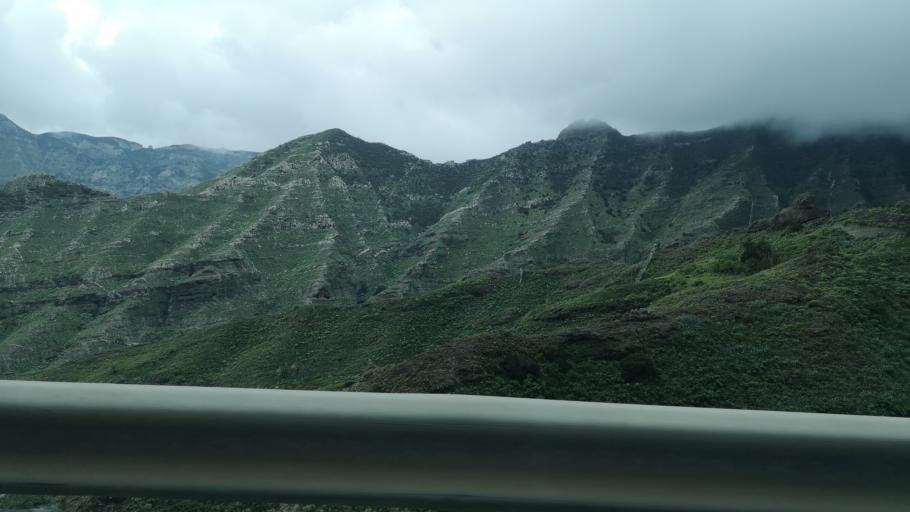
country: ES
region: Canary Islands
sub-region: Provincia de Santa Cruz de Tenerife
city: Hermigua
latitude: 28.1320
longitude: -17.1793
